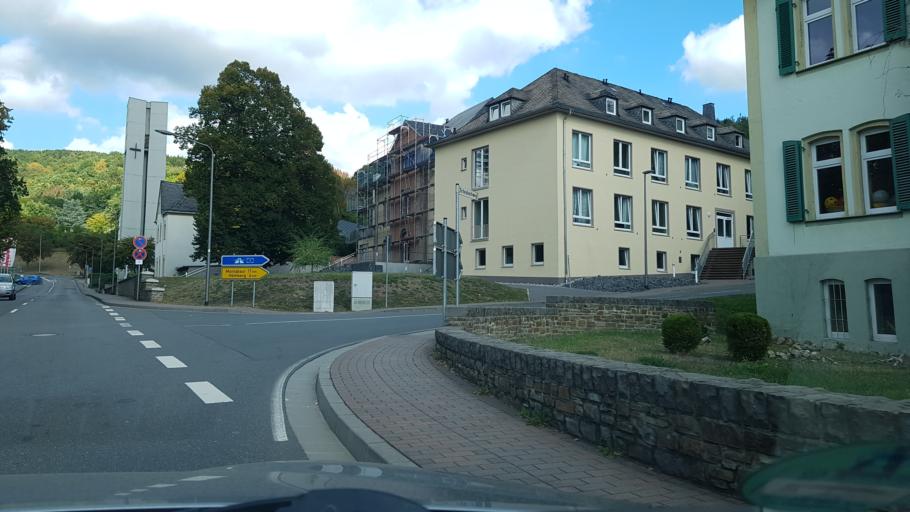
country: DE
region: Rheinland-Pfalz
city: Nassau
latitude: 50.3160
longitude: 7.7950
